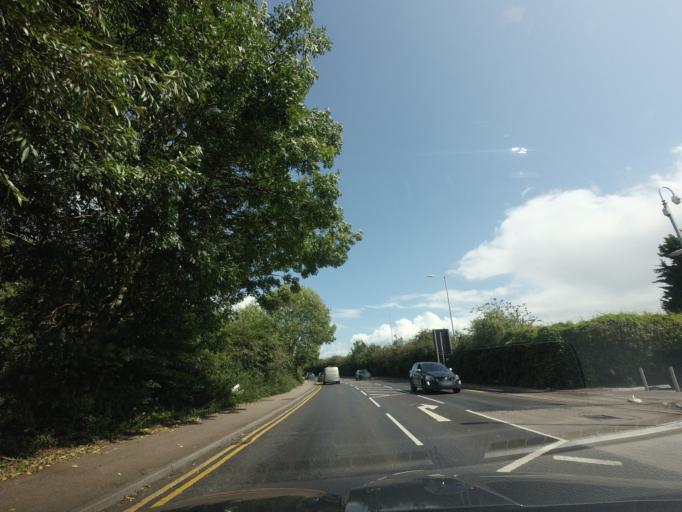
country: GB
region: England
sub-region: Kent
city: Tonbridge
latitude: 51.1921
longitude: 0.2869
